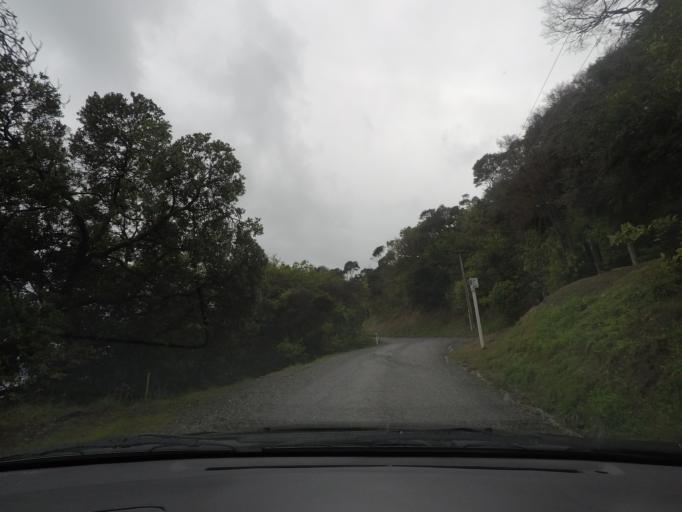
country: NZ
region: Auckland
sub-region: Auckland
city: Warkworth
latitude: -36.4848
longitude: 174.7247
